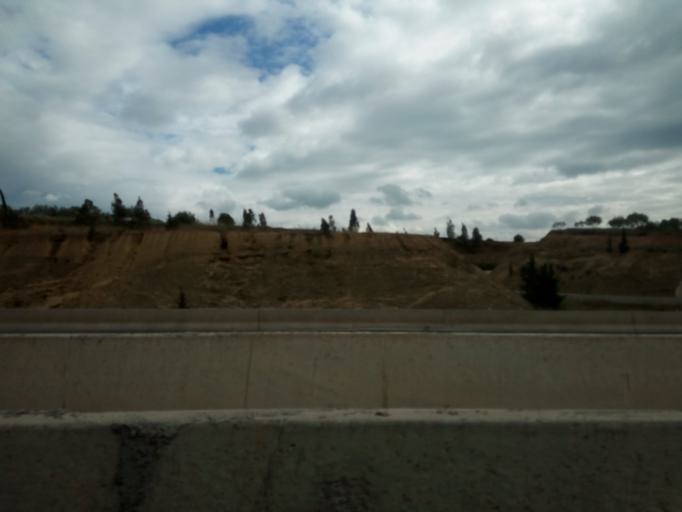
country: DZ
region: Bouira
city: Chorfa
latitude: 36.3159
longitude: 4.1570
